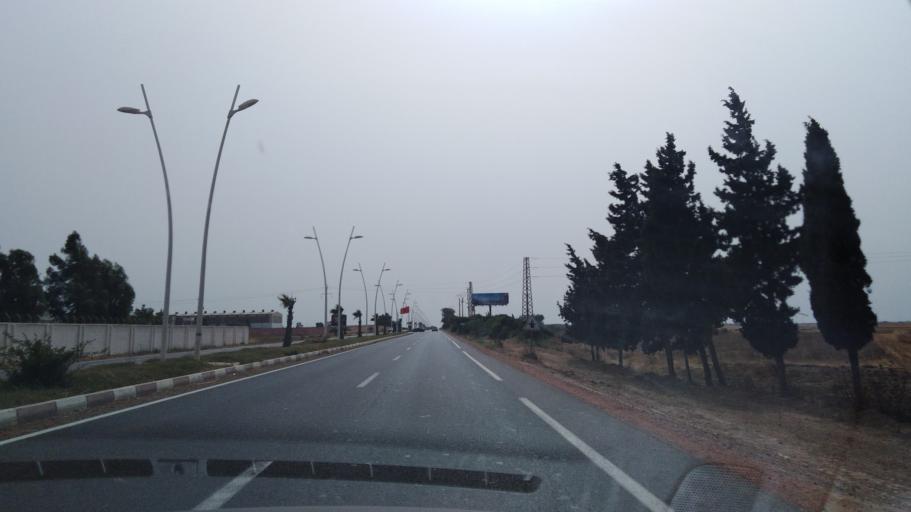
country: MA
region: Chaouia-Ouardigha
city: Nouaseur
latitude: 33.3991
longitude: -7.5781
